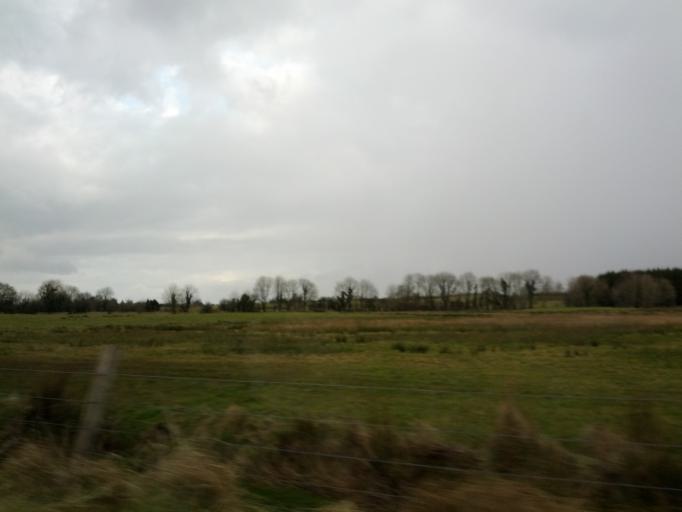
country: IE
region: Connaught
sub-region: County Galway
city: Athenry
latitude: 53.3974
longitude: -8.6111
